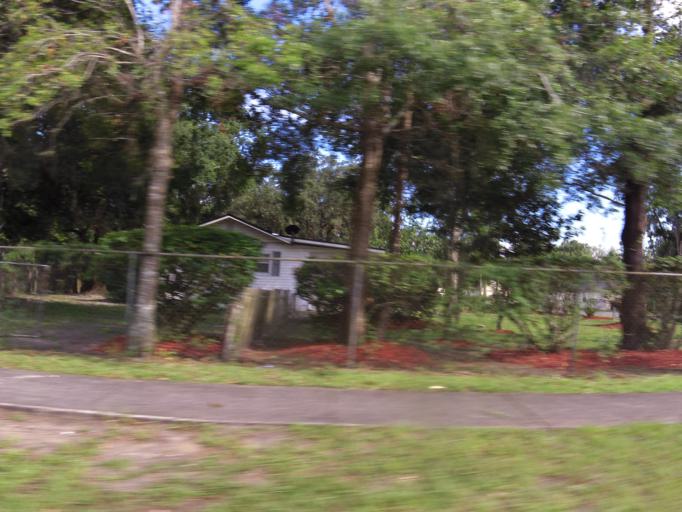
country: US
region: Florida
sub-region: Clay County
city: Green Cove Springs
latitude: 29.9937
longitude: -81.6969
